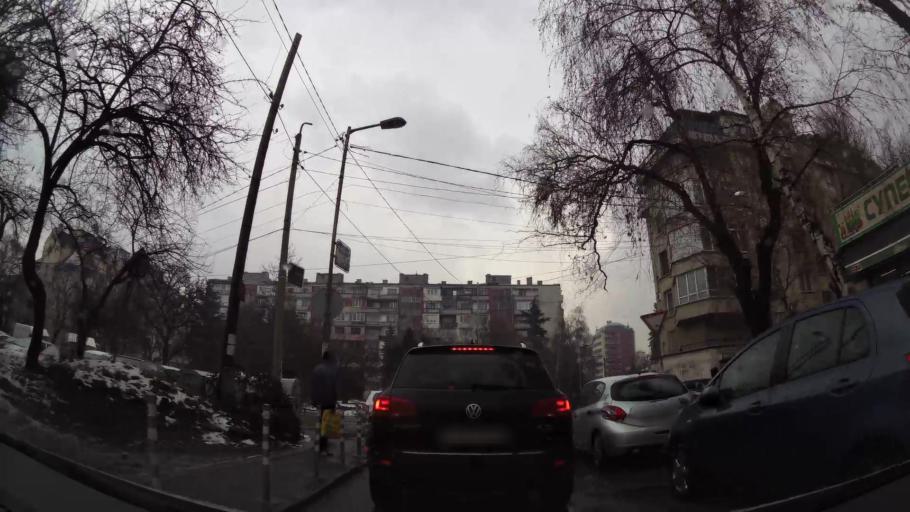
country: BG
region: Sofia-Capital
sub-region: Stolichna Obshtina
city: Sofia
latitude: 42.6718
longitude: 23.2904
